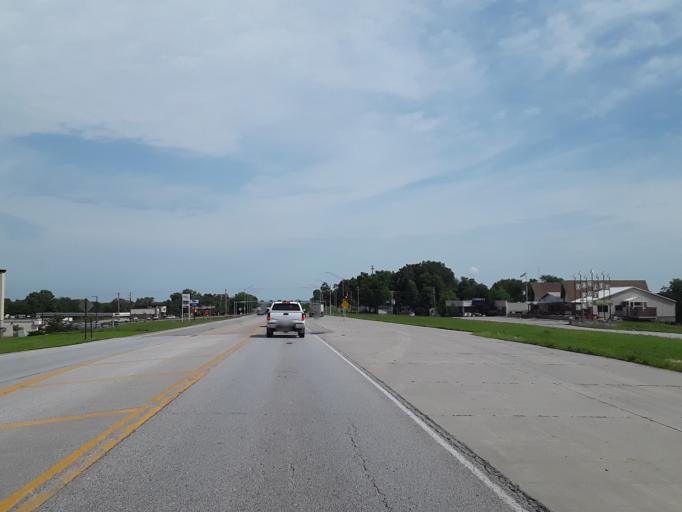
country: US
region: Nebraska
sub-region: Cass County
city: Plattsmouth
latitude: 41.0103
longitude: -95.9086
